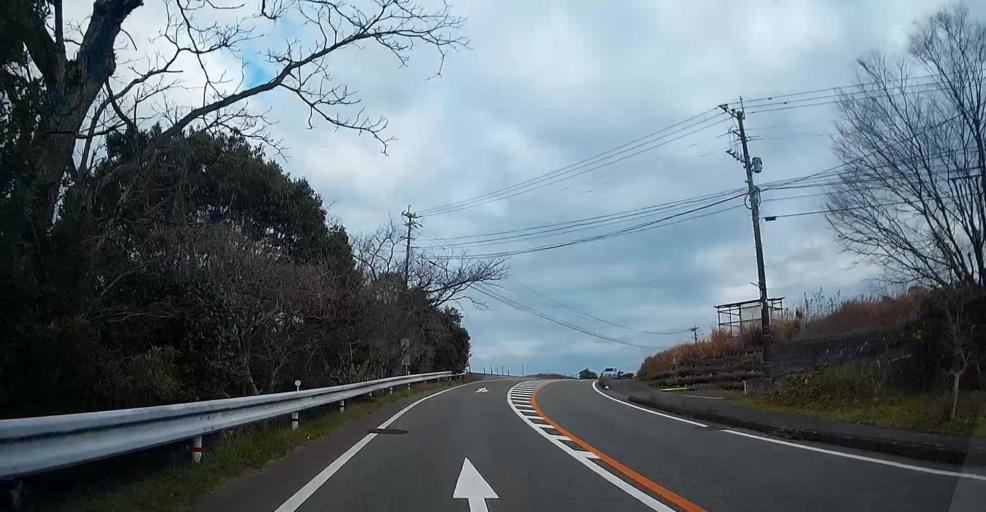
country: JP
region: Kumamoto
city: Hondo
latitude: 32.4586
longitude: 130.2233
